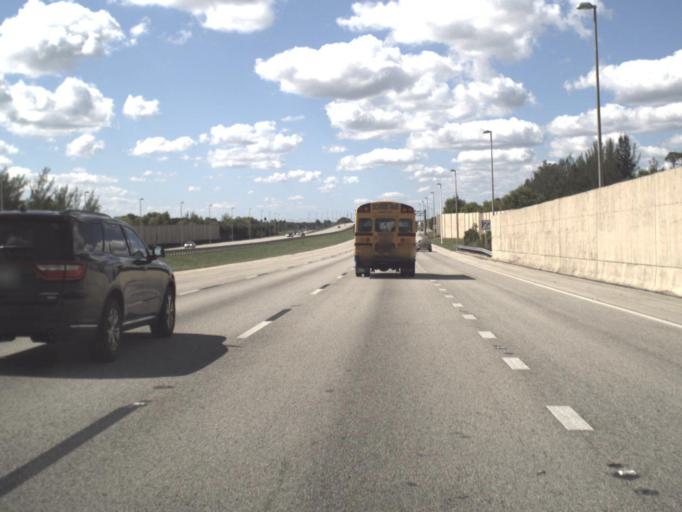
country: US
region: Florida
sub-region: Broward County
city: Parkland
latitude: 26.3020
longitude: -80.2397
